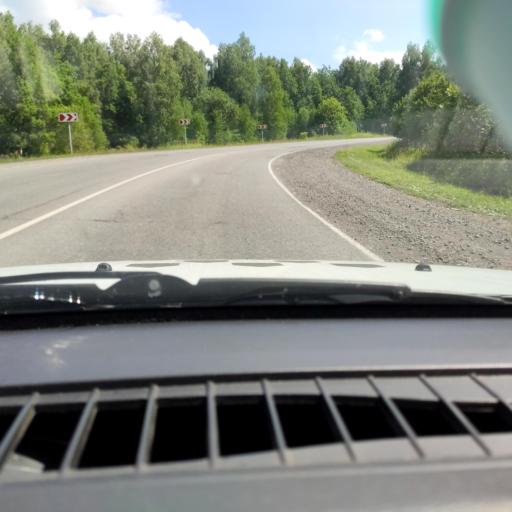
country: RU
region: Bashkortostan
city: Verkhniye Kigi
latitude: 55.3847
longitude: 58.6746
